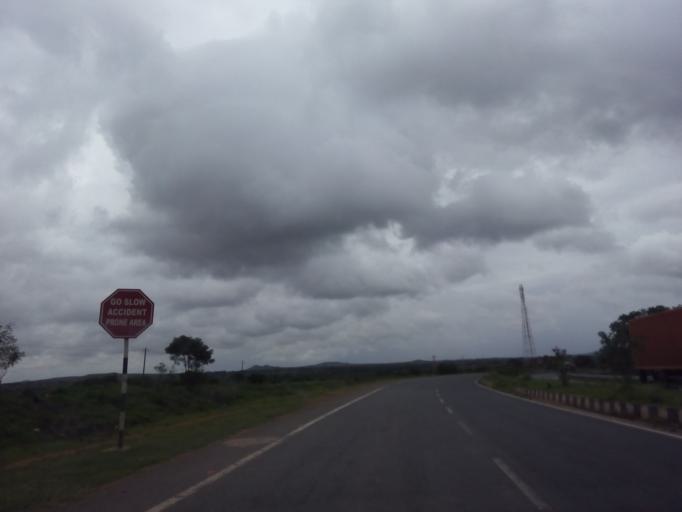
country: IN
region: Karnataka
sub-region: Haveri
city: Haveri
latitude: 14.7613
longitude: 75.4376
